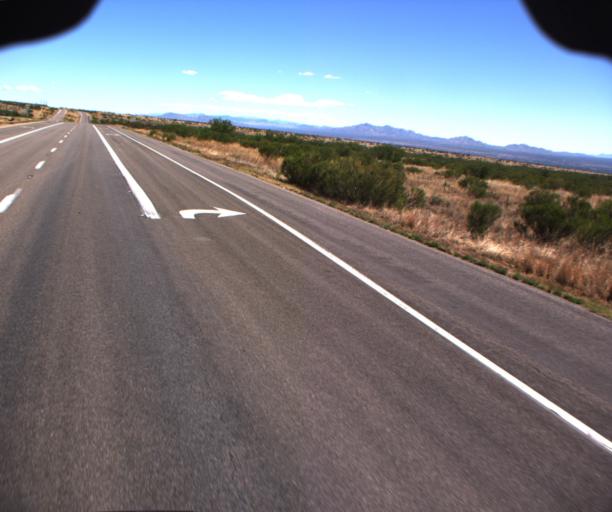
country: US
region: Arizona
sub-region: Cochise County
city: Whetstone
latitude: 31.8339
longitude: -110.3437
